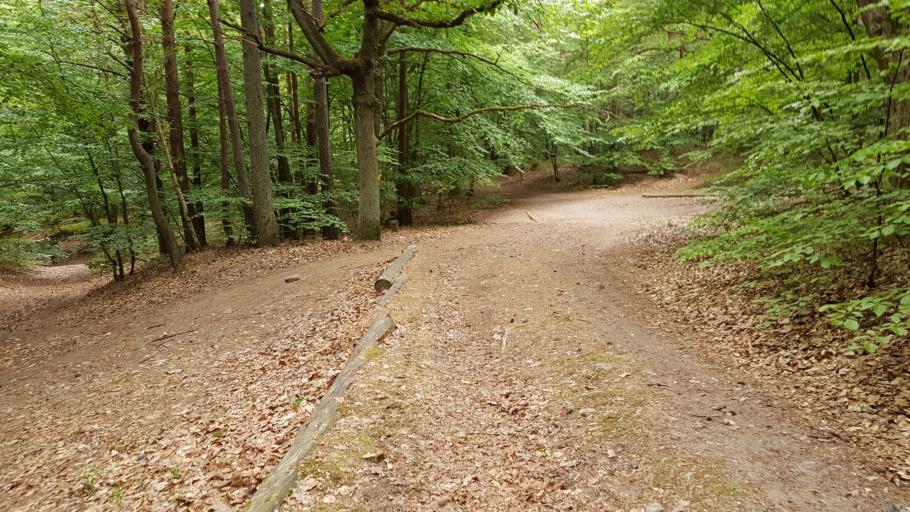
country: PL
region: West Pomeranian Voivodeship
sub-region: Powiat kamienski
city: Miedzyzdroje
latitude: 53.9327
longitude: 14.4620
